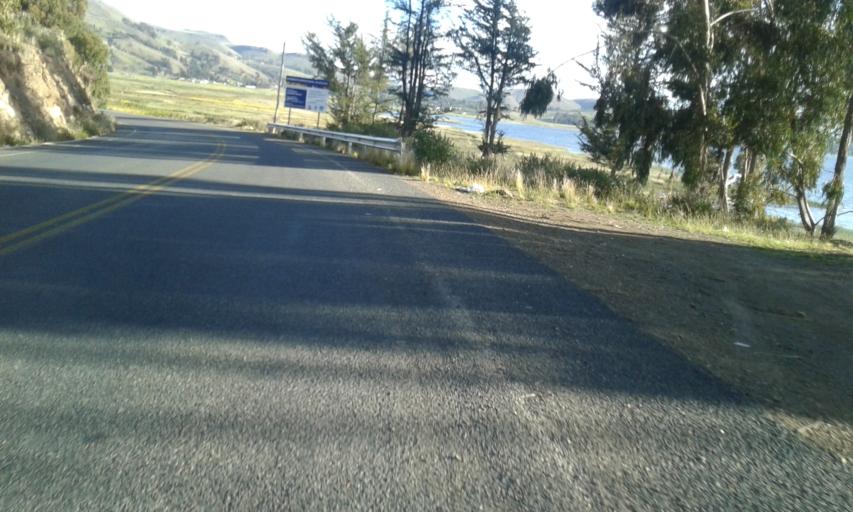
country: BO
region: La Paz
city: Achacachi
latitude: -16.0406
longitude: -68.8351
